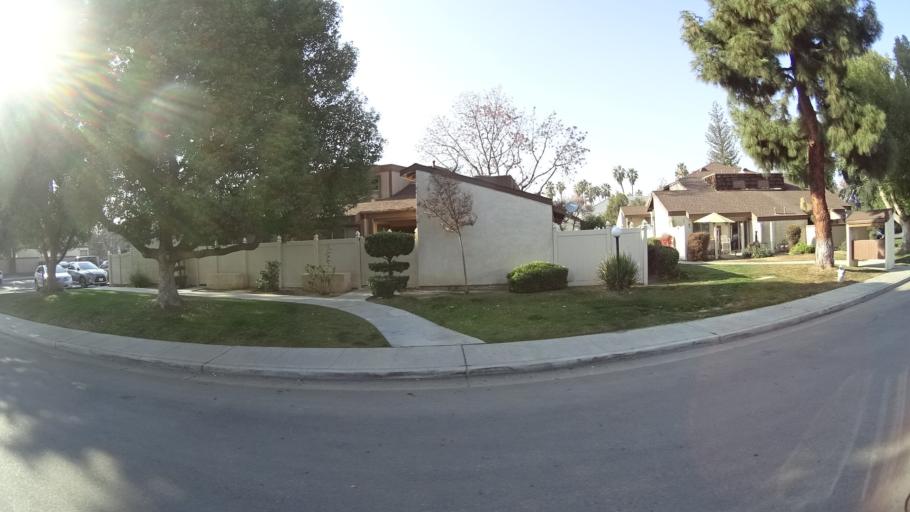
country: US
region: California
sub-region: Kern County
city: Bakersfield
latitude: 35.3592
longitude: -119.0575
